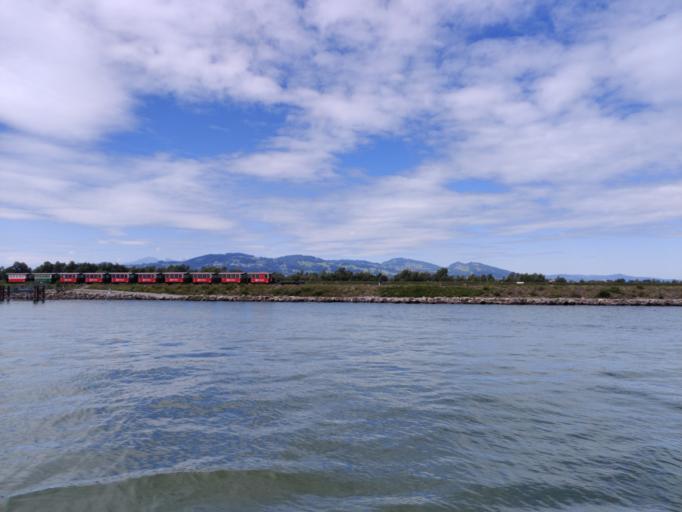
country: AT
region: Vorarlberg
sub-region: Politischer Bezirk Bregenz
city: Hard
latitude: 47.5074
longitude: 9.6702
